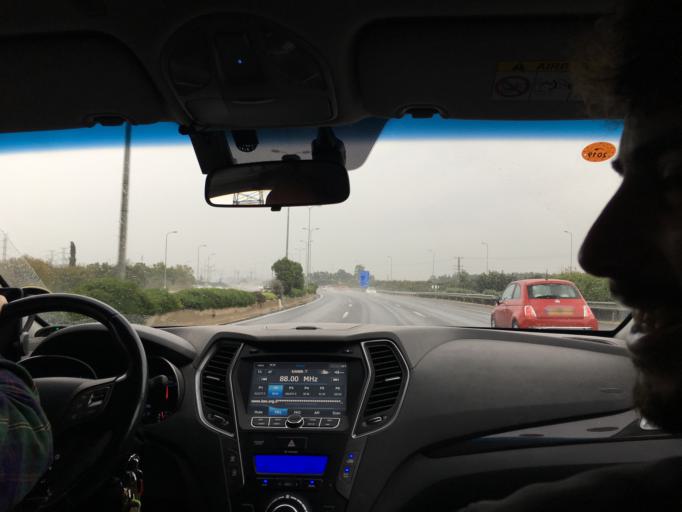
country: IL
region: Central District
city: Petah Tiqwa
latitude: 32.1176
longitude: 34.8786
